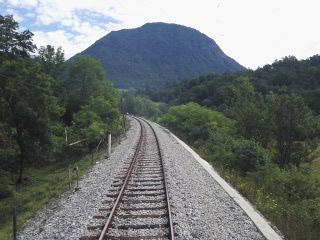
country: SI
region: Cerkno
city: Cerkno
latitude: 46.1562
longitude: 13.8672
